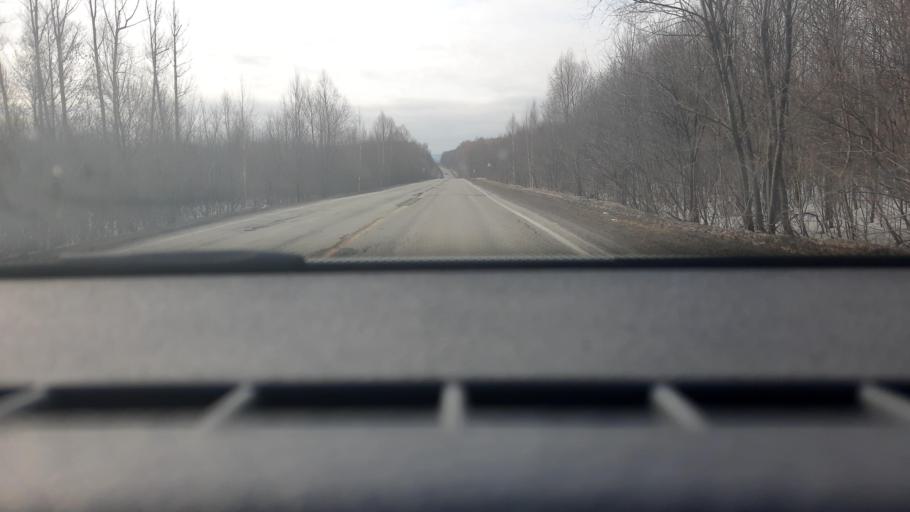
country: RU
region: Chelyabinsk
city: Asha
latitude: 54.9210
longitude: 57.2908
